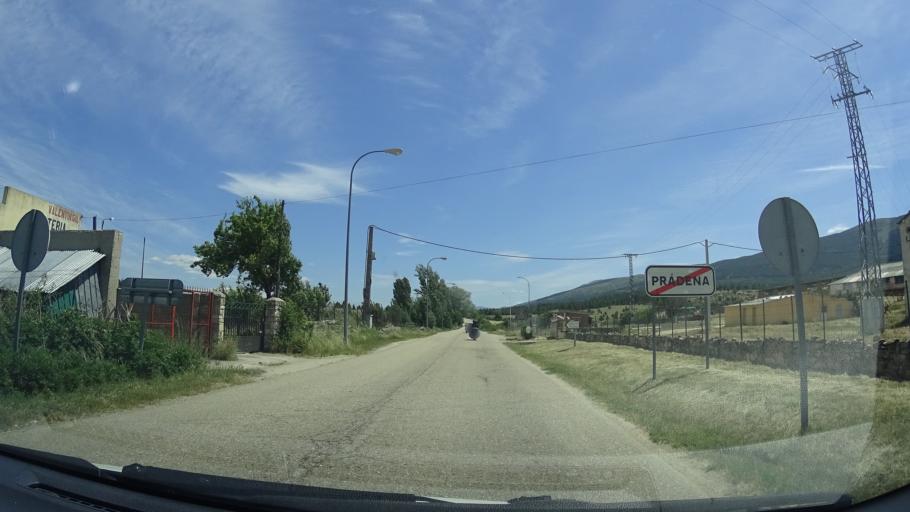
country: ES
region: Castille and Leon
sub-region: Provincia de Segovia
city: Pradena
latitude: 41.1416
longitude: -3.6818
